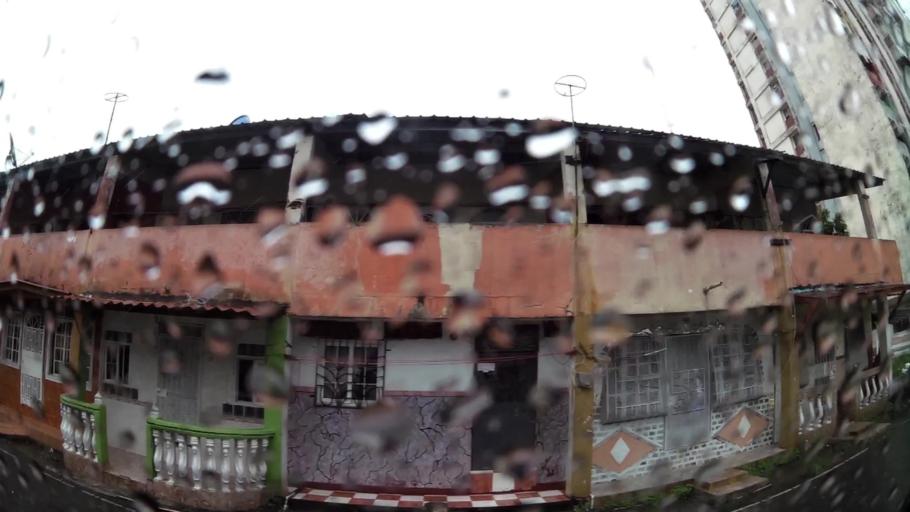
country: PA
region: Colon
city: Colon
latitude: 9.3618
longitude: -79.9040
